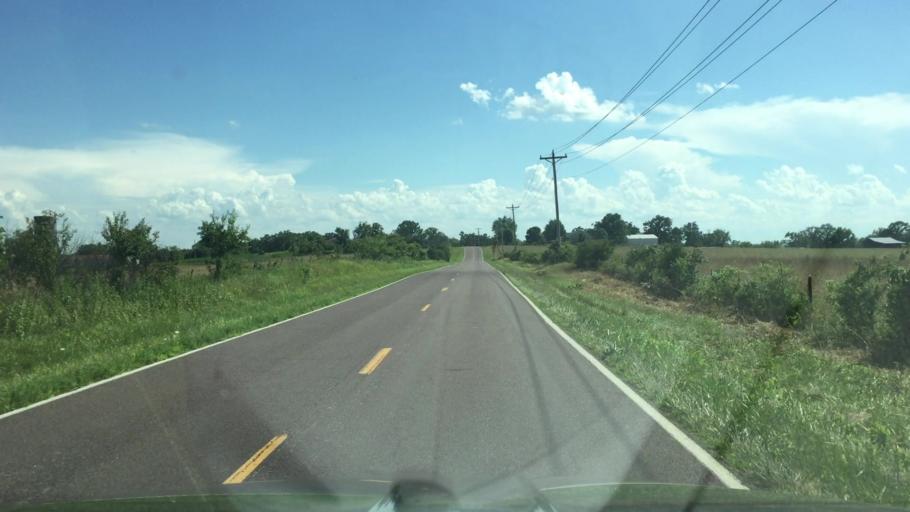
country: US
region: Missouri
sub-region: Miller County
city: Tuscumbia
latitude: 38.0997
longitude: -92.4777
